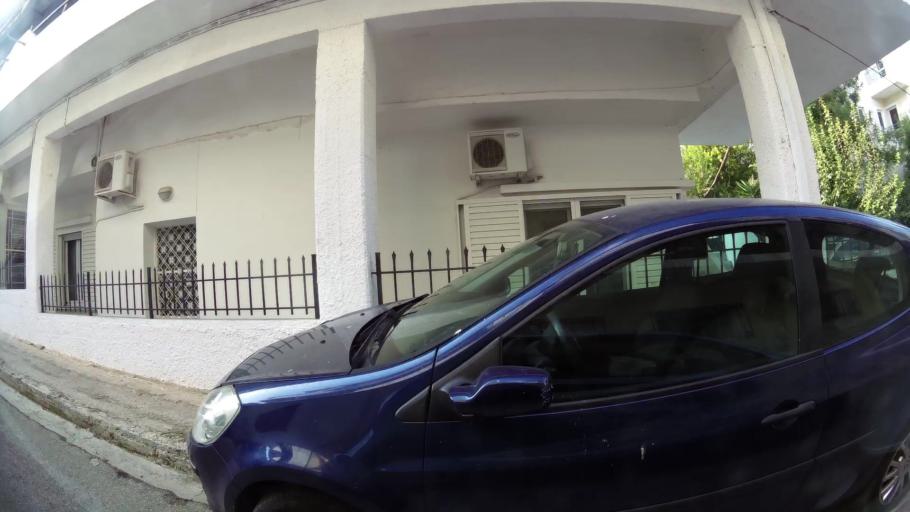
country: GR
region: Attica
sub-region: Nomarchia Athinas
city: Agia Paraskevi
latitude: 38.0112
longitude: 23.8357
